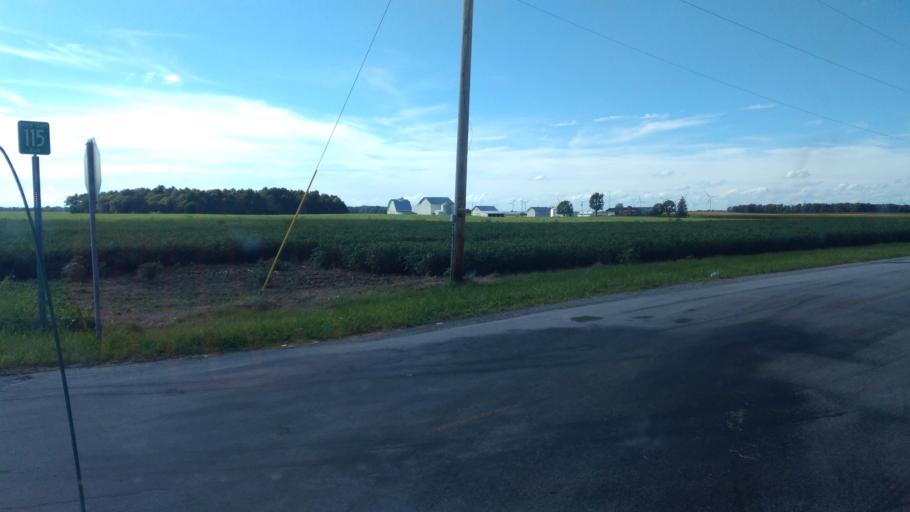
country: US
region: Ohio
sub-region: Hardin County
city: Kenton
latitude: 40.7324
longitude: -83.6907
